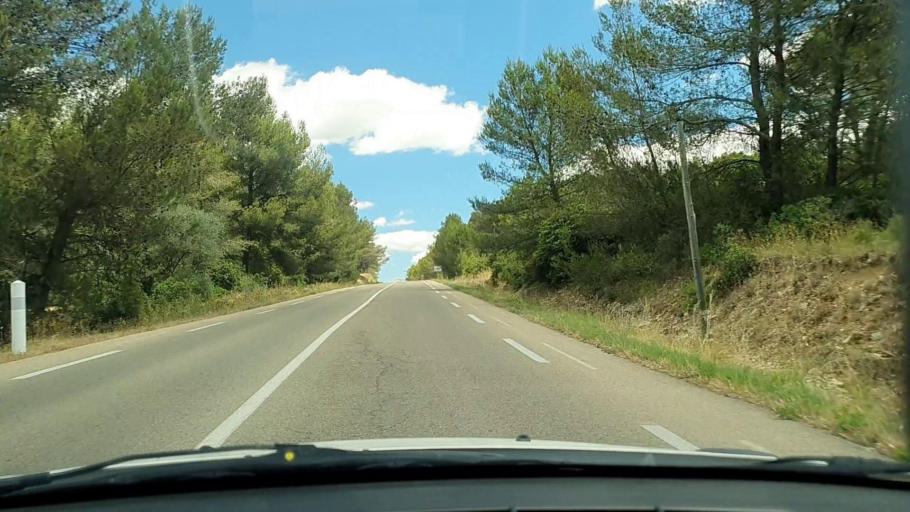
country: FR
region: Languedoc-Roussillon
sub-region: Departement du Gard
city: Poulx
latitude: 43.8721
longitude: 4.4098
